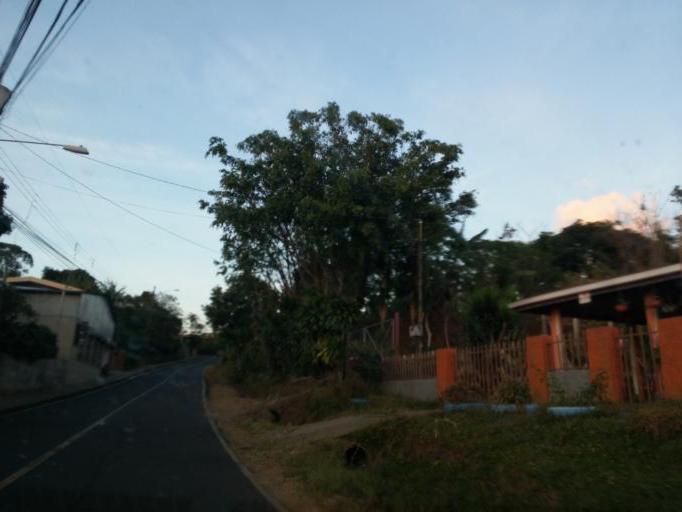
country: CR
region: Alajuela
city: Sabanilla
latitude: 10.0716
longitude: -84.2167
